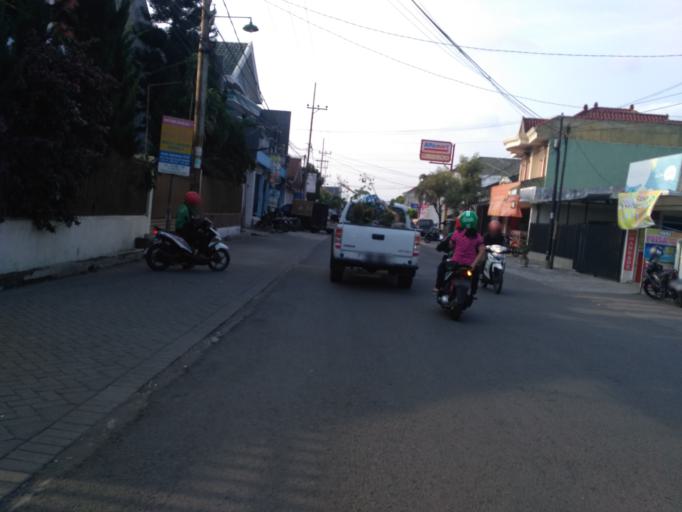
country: ID
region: East Java
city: Malang
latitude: -7.9386
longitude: 112.6371
